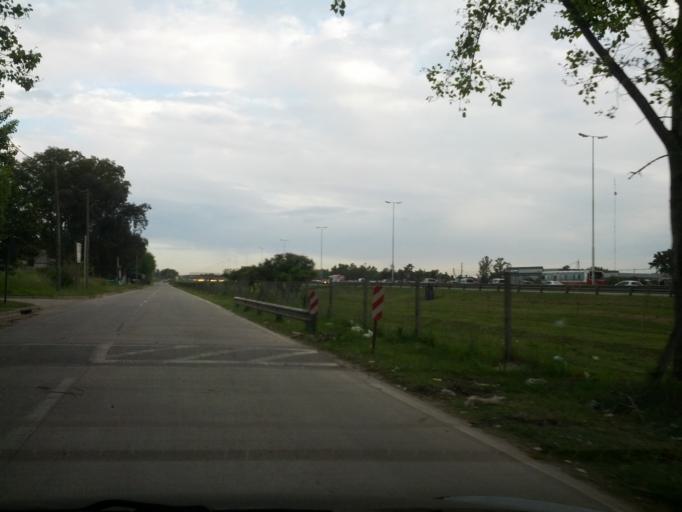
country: AR
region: Buenos Aires
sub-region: Partido de General Rodriguez
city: General Rodriguez
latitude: -34.6111
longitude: -58.8651
